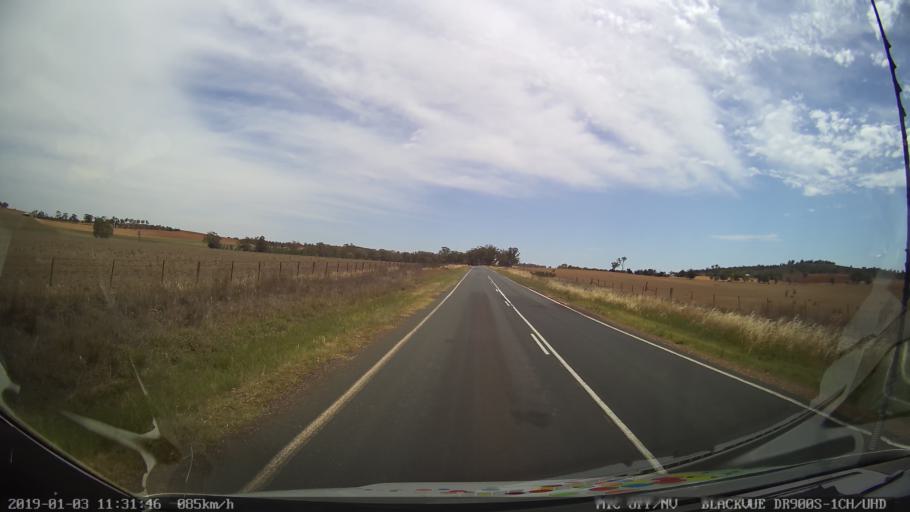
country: AU
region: New South Wales
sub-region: Weddin
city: Grenfell
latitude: -33.9666
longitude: 148.1817
